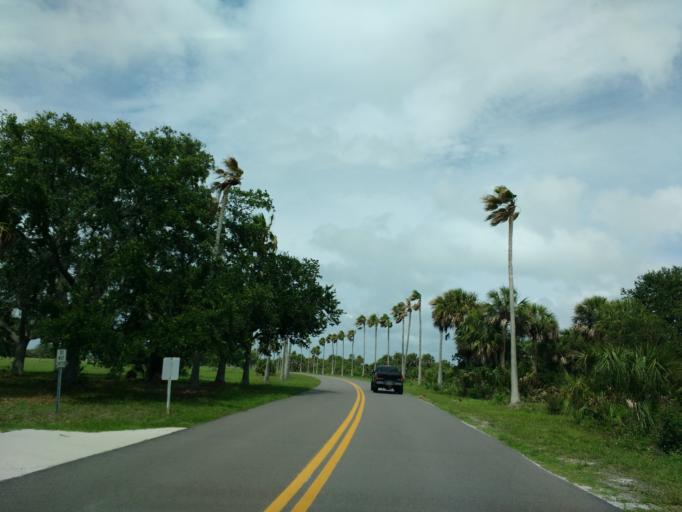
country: US
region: Florida
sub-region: Pinellas County
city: Tierra Verde
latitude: 27.6137
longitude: -82.7343
